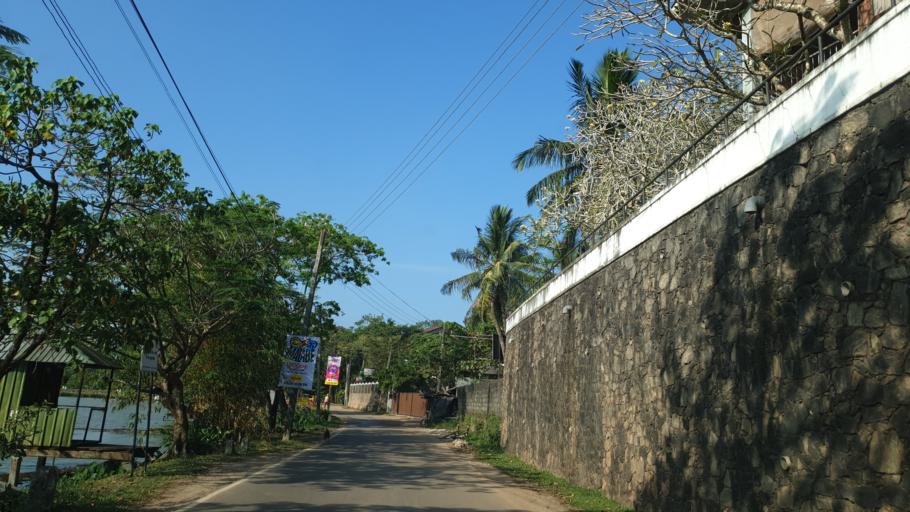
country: LK
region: Western
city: Battaramulla South
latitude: 6.8878
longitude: 79.9477
